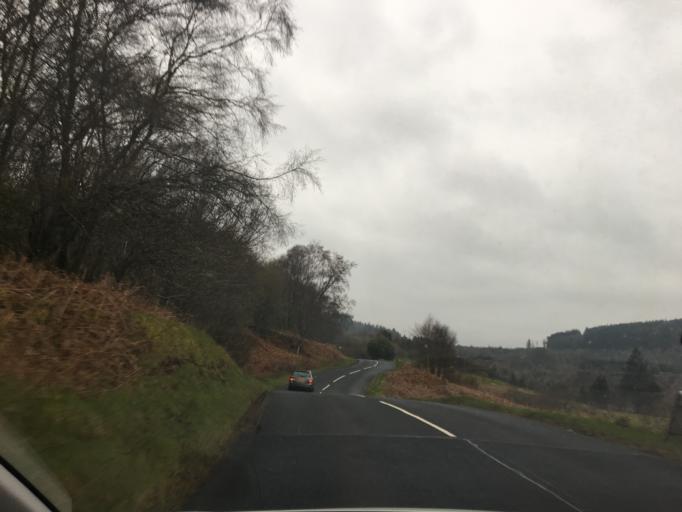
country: GB
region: Scotland
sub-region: North Ayrshire
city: Lamlash
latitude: 55.5460
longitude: -5.1340
